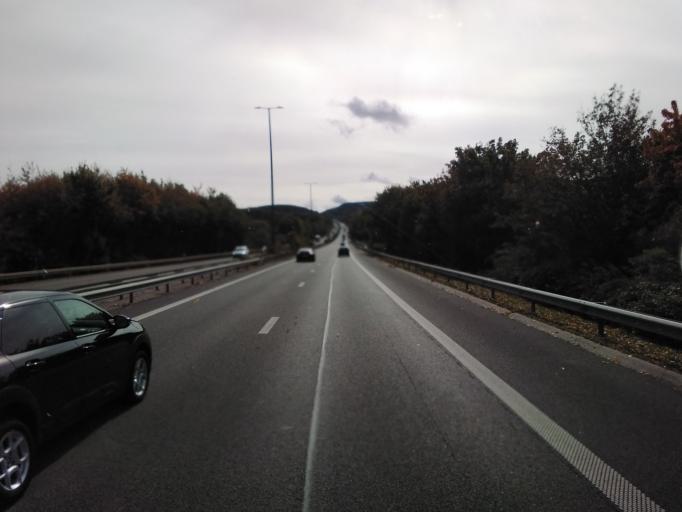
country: BE
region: Wallonia
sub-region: Province du Luxembourg
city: Wellin
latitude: 50.0878
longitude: 5.1628
